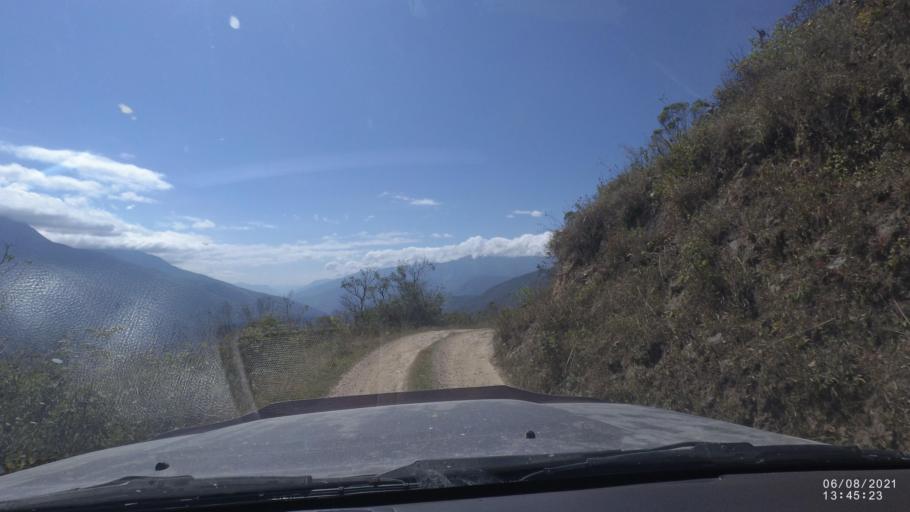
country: BO
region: La Paz
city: Quime
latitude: -16.6721
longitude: -66.7320
